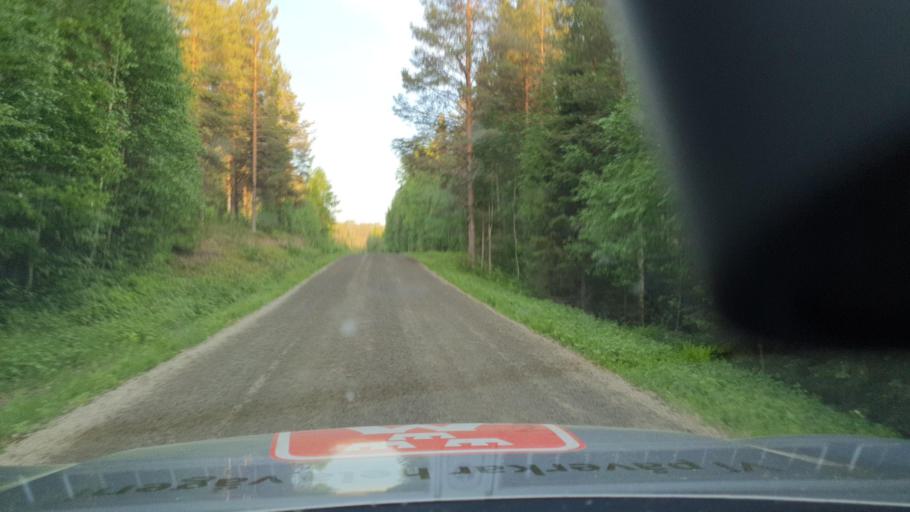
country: SE
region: Norrbotten
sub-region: Bodens Kommun
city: Boden
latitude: 66.1543
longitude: 21.5574
